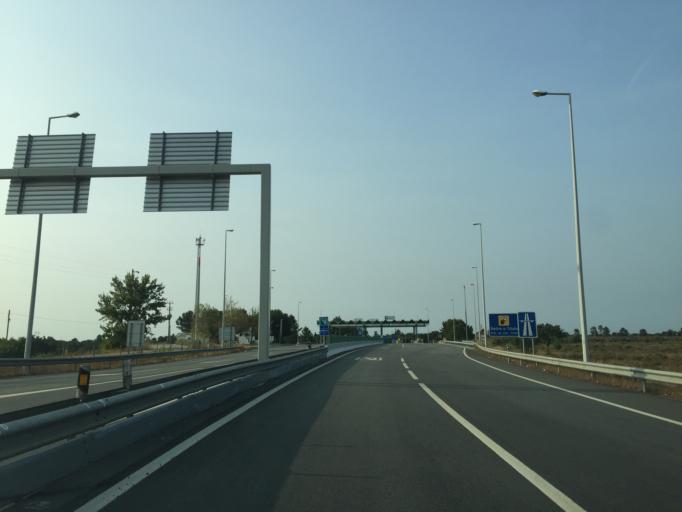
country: PT
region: Setubal
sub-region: Setubal
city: Setubal
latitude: 38.5961
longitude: -8.6735
